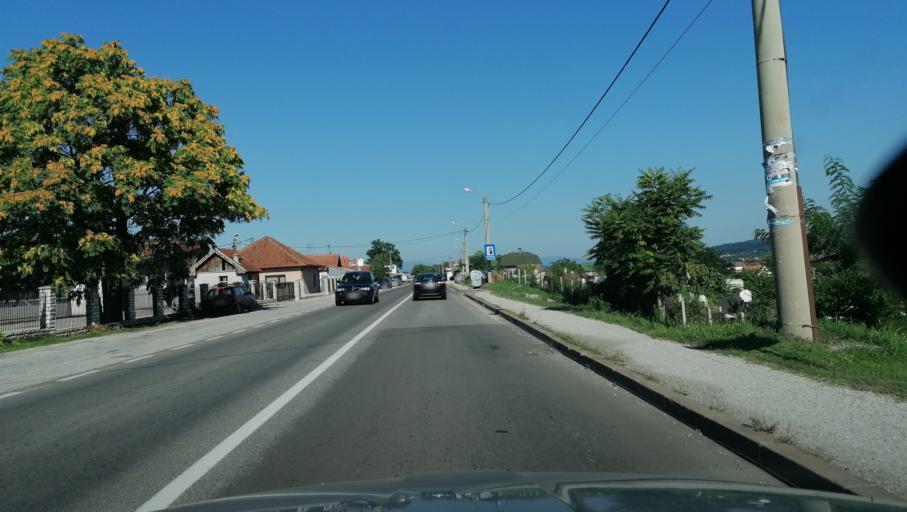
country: RS
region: Central Serbia
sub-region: Raski Okrug
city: Kraljevo
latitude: 43.6964
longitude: 20.6036
